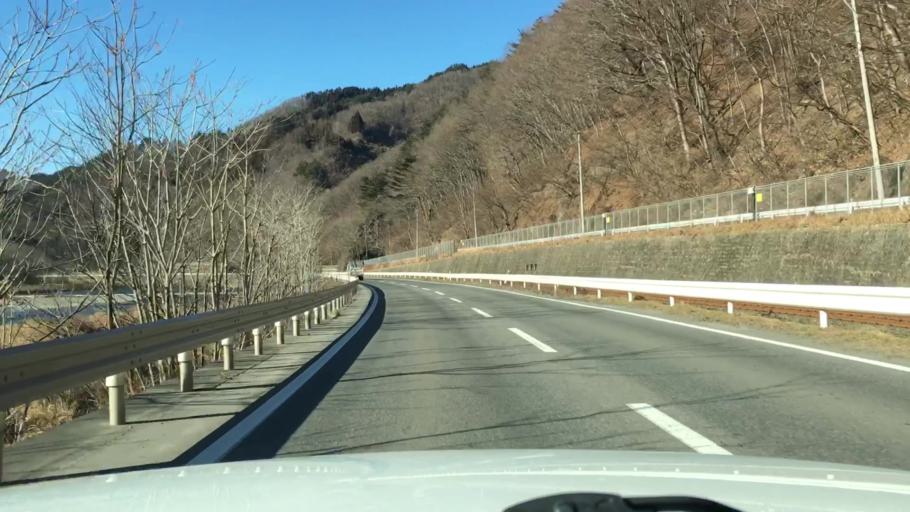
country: JP
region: Iwate
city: Miyako
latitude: 39.6325
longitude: 141.8526
